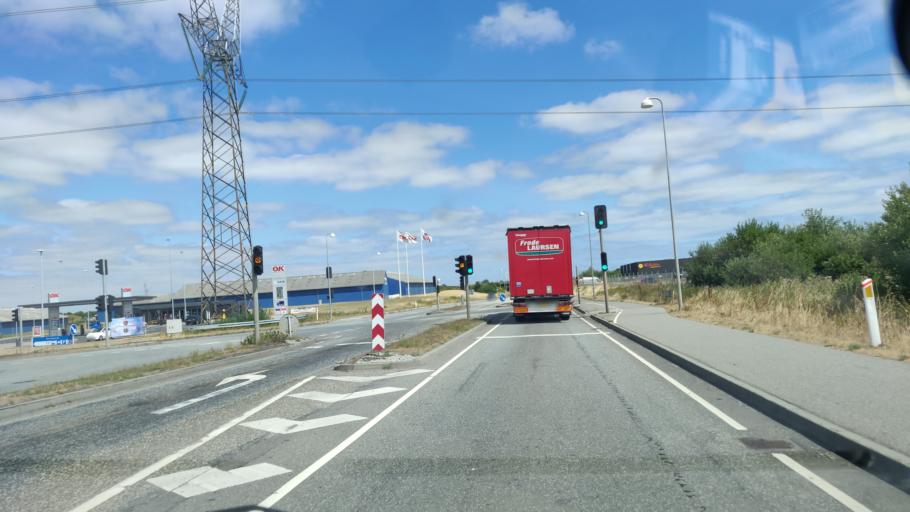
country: DK
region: South Denmark
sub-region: Fredericia Kommune
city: Taulov
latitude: 55.5417
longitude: 9.6423
